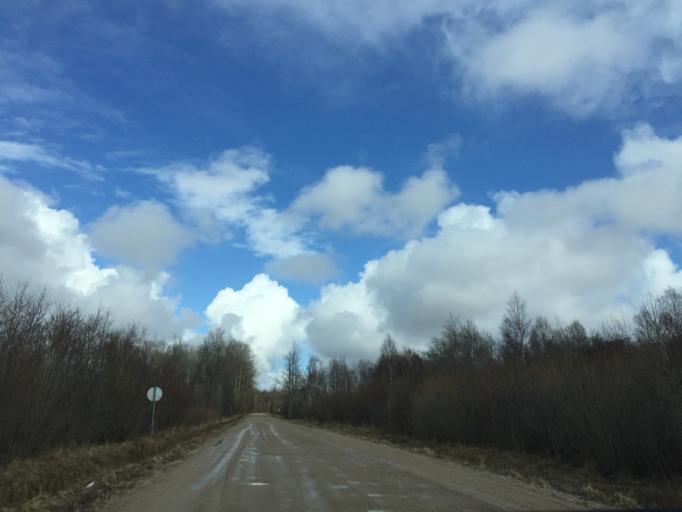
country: EE
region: Laeaene
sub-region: Lihula vald
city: Lihula
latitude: 58.7163
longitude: 23.8223
